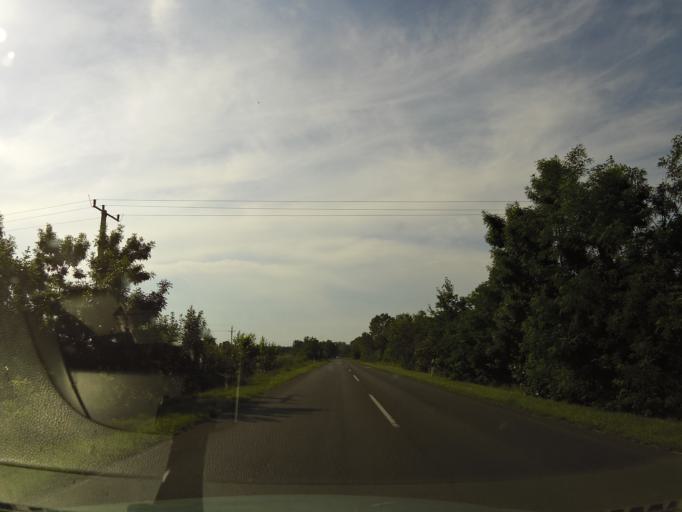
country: HU
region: Csongrad
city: Balastya
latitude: 46.3896
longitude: 20.0333
